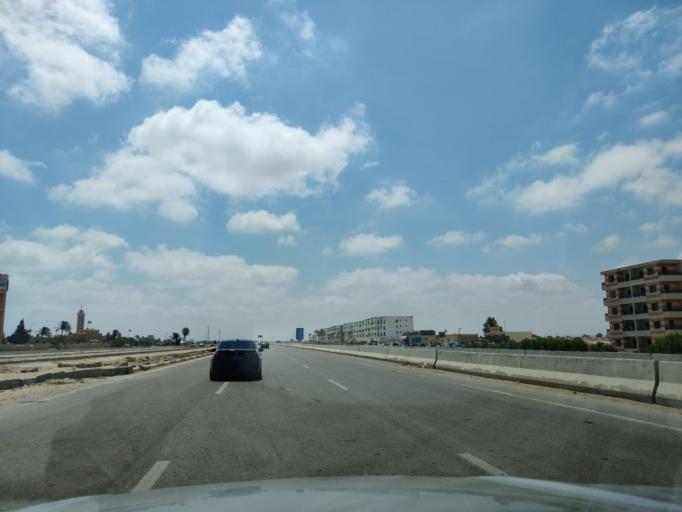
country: EG
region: Muhafazat Matruh
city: Al `Alamayn
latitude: 30.8179
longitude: 29.0273
